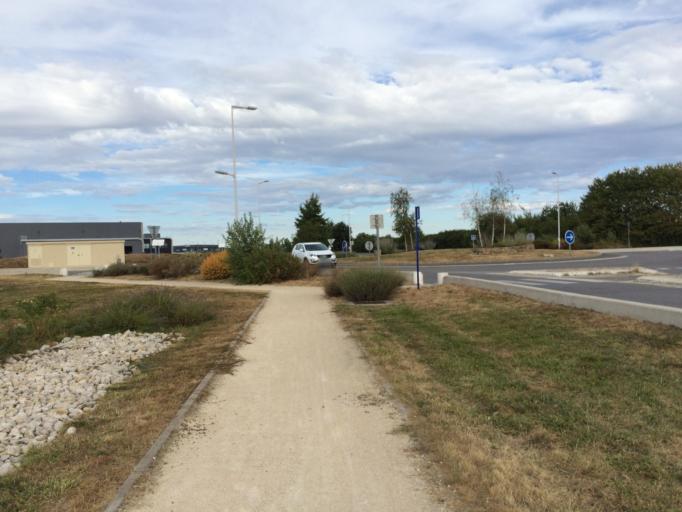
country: FR
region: Ile-de-France
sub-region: Departement de l'Essonne
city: Chilly-Mazarin
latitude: 48.7187
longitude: 2.3286
